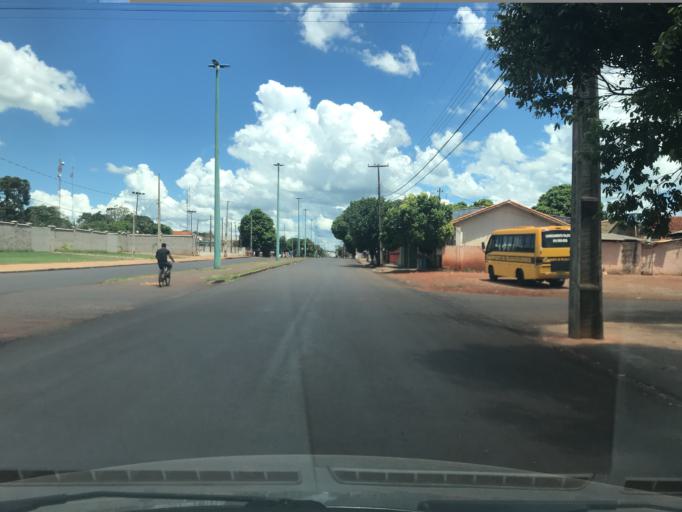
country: BR
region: Parana
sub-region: Palotina
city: Palotina
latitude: -24.2712
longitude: -53.8417
